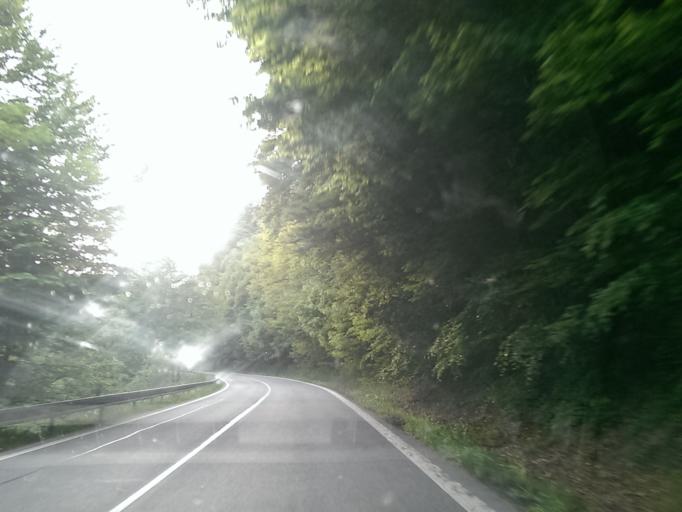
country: CZ
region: Liberecky
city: Zelezny Brod
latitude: 50.6462
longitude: 15.2297
